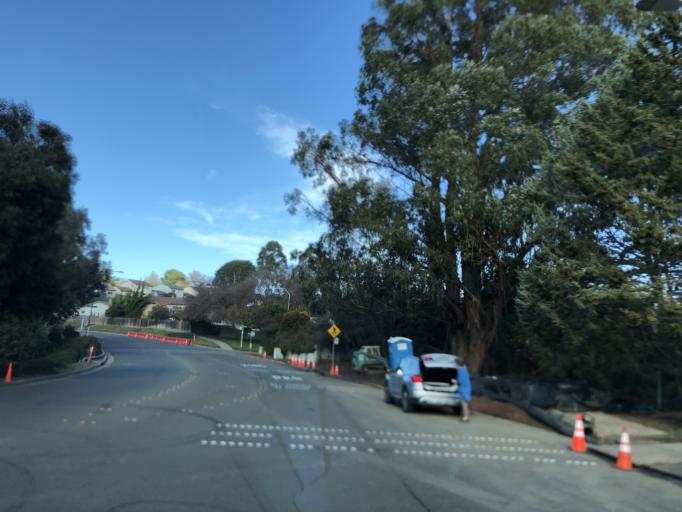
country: US
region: California
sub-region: Contra Costa County
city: El Sobrante
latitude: 37.9796
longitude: -122.3093
